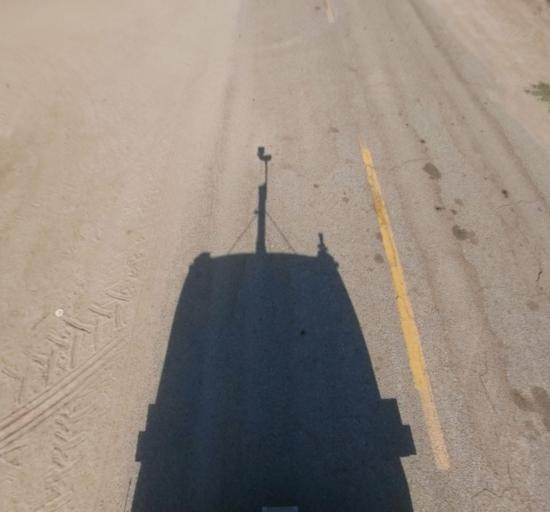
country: US
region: California
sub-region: Madera County
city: Madera
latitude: 36.9165
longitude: -120.1196
